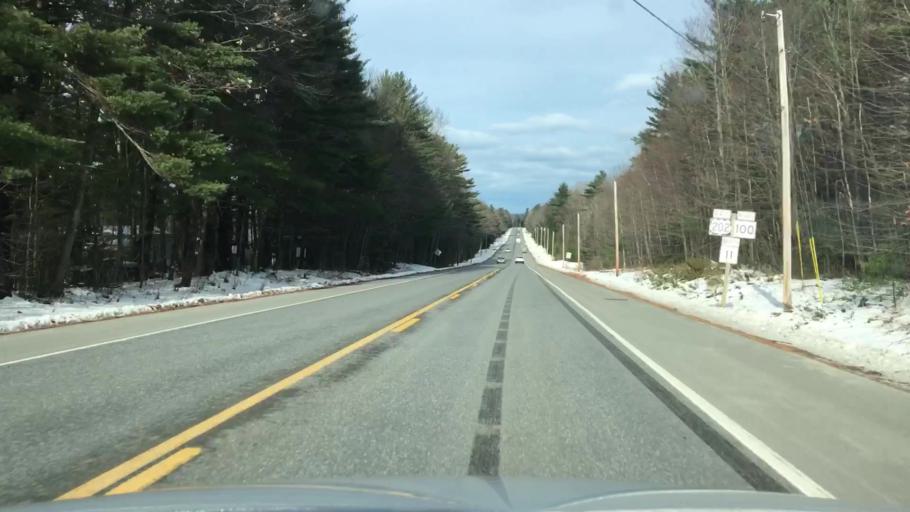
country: US
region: Maine
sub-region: Kennebec County
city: Monmouth
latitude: 44.2354
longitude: -70.0701
